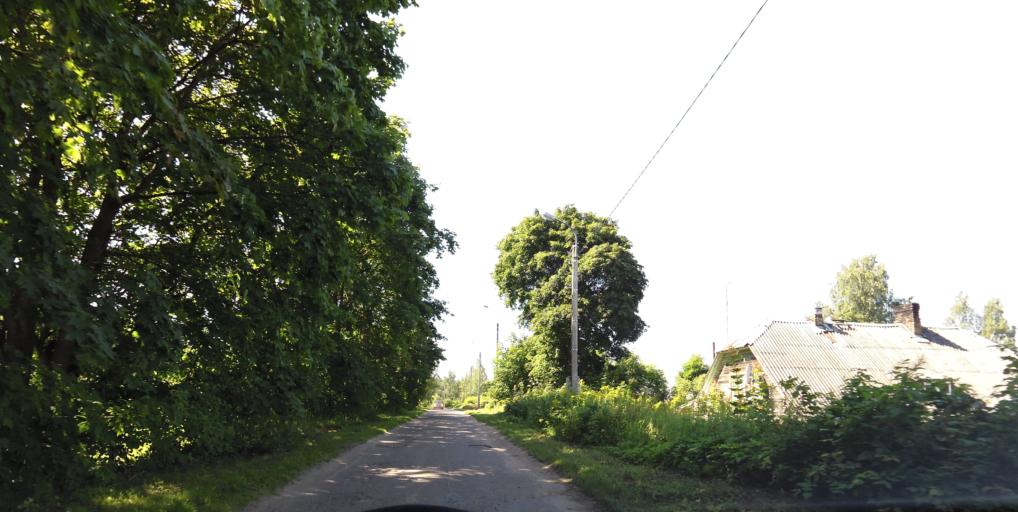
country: LT
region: Vilnius County
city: Rasos
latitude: 54.6784
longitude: 25.3530
